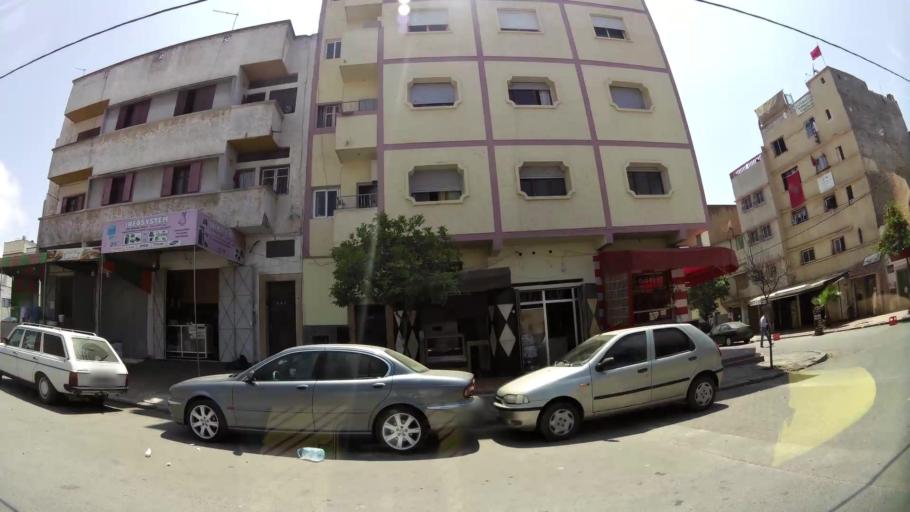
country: MA
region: Rabat-Sale-Zemmour-Zaer
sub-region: Skhirate-Temara
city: Temara
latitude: 33.9735
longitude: -6.8891
